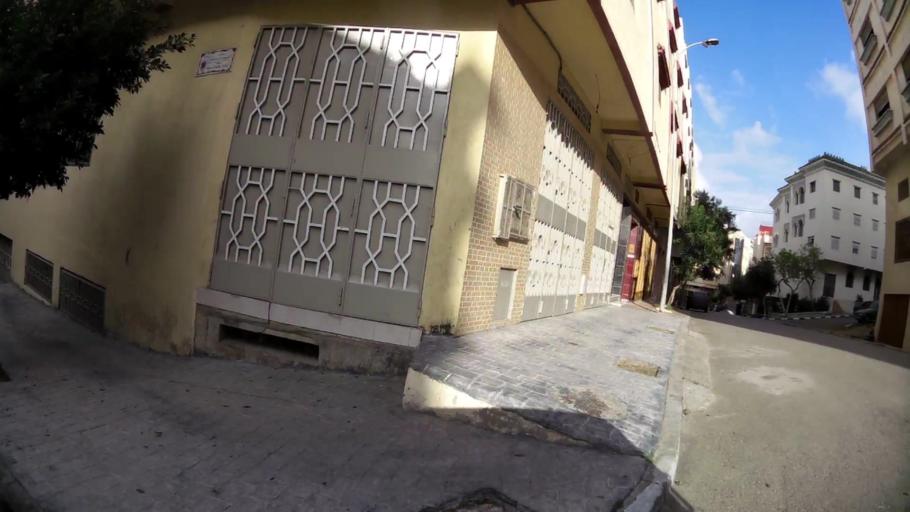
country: MA
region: Tanger-Tetouan
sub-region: Tanger-Assilah
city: Tangier
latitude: 35.7627
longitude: -5.8354
